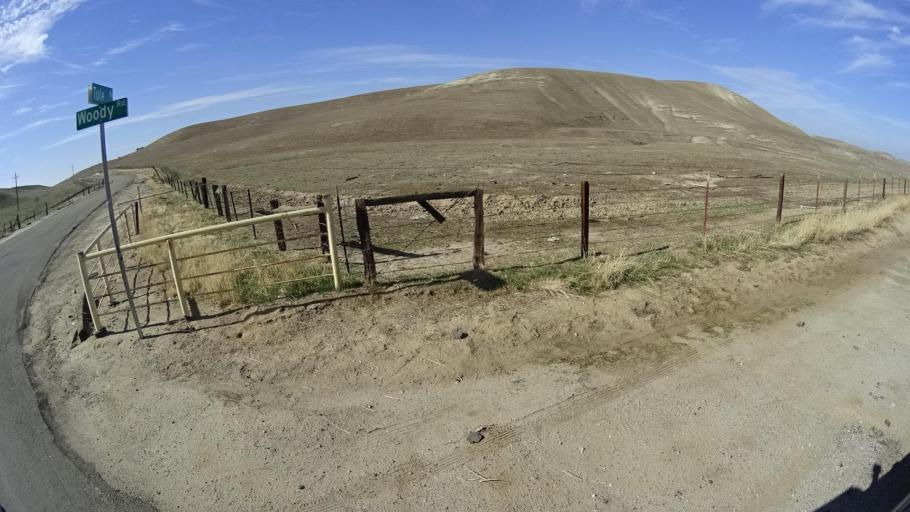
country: US
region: California
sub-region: Tulare County
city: Richgrove
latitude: 35.6380
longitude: -118.9435
